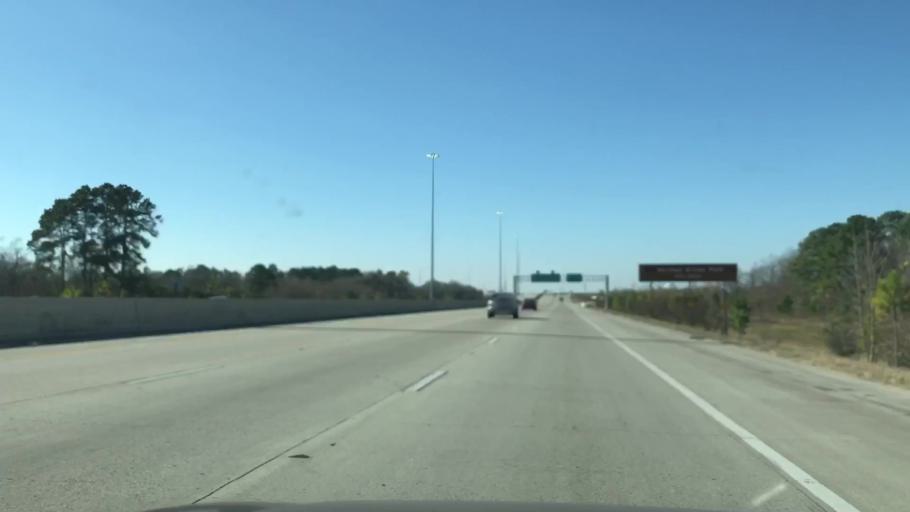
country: US
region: Texas
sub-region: Harris County
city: Jacinto City
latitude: 29.7884
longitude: -95.2409
